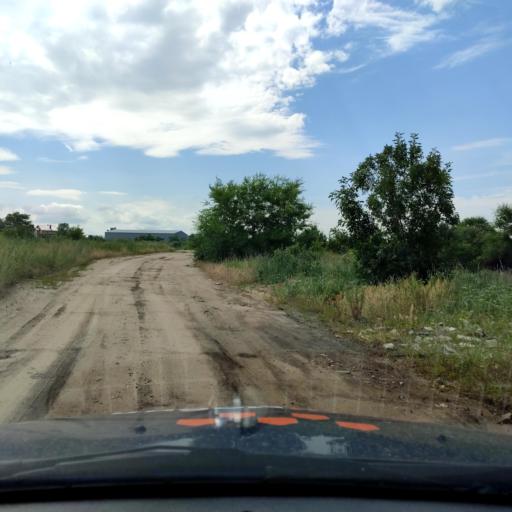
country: RU
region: Voronezj
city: Pridonskoy
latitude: 51.6374
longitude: 39.1089
